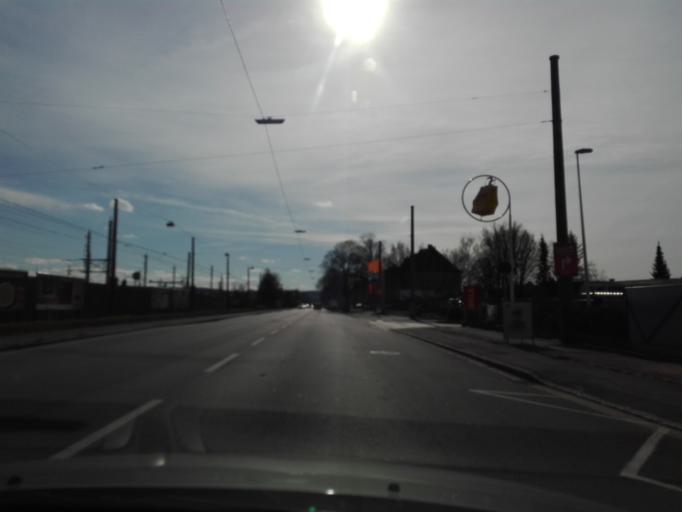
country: AT
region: Upper Austria
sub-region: Linz Stadt
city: Linz
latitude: 48.2635
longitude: 14.3186
